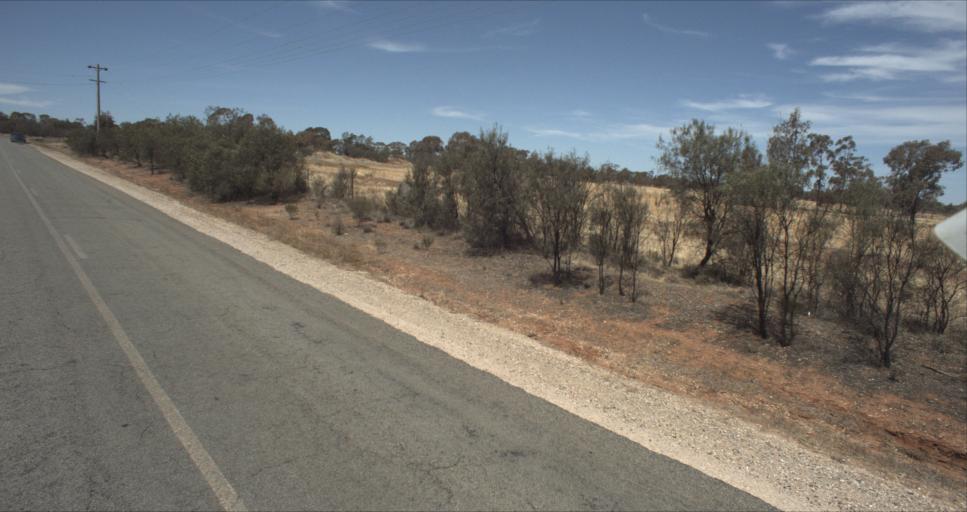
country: AU
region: New South Wales
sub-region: Leeton
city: Leeton
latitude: -34.5858
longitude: 146.4287
